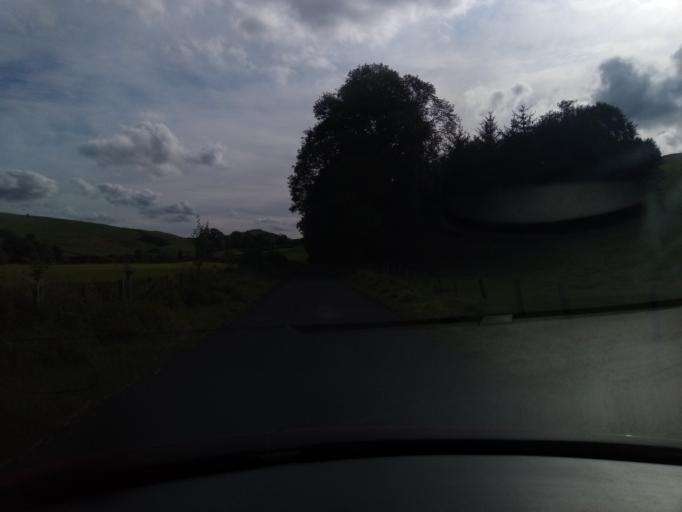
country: GB
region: Scotland
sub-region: The Scottish Borders
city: Kelso
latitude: 55.4895
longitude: -2.3481
